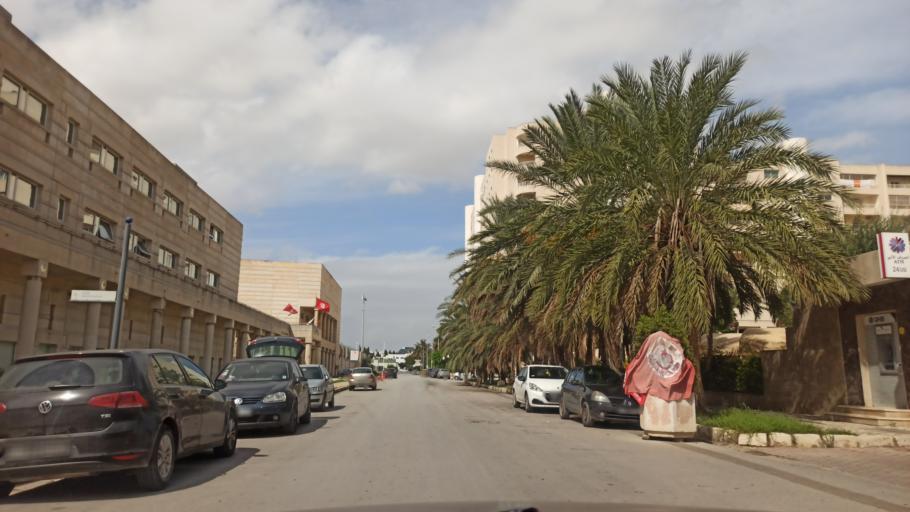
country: TN
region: Ariana
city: Ariana
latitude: 36.8477
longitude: 10.1904
